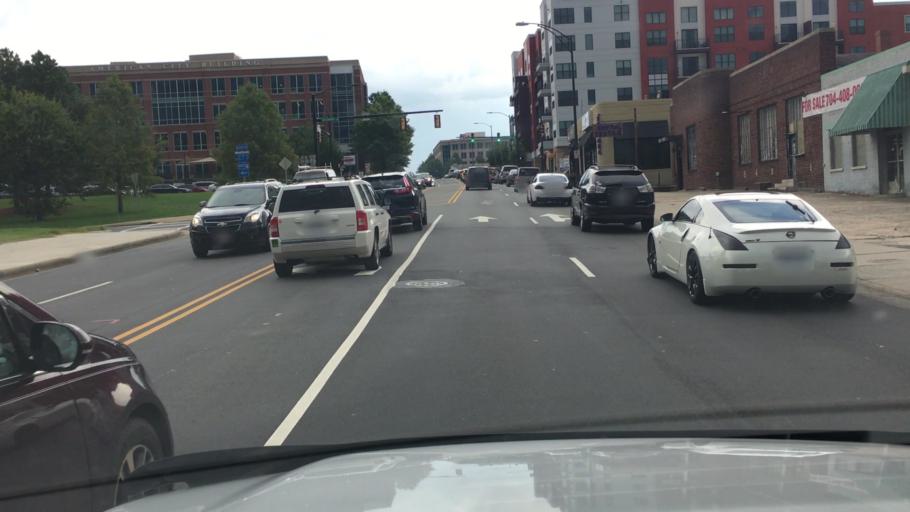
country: US
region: North Carolina
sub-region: Mecklenburg County
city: Charlotte
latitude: 35.2229
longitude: -80.8533
